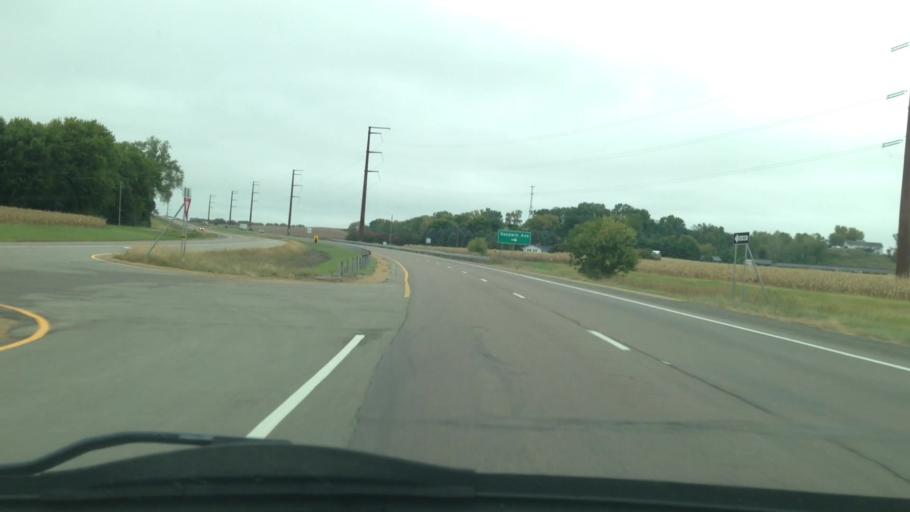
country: US
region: Minnesota
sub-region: Goodhue County
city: Cannon Falls
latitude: 44.5635
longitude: -92.9525
